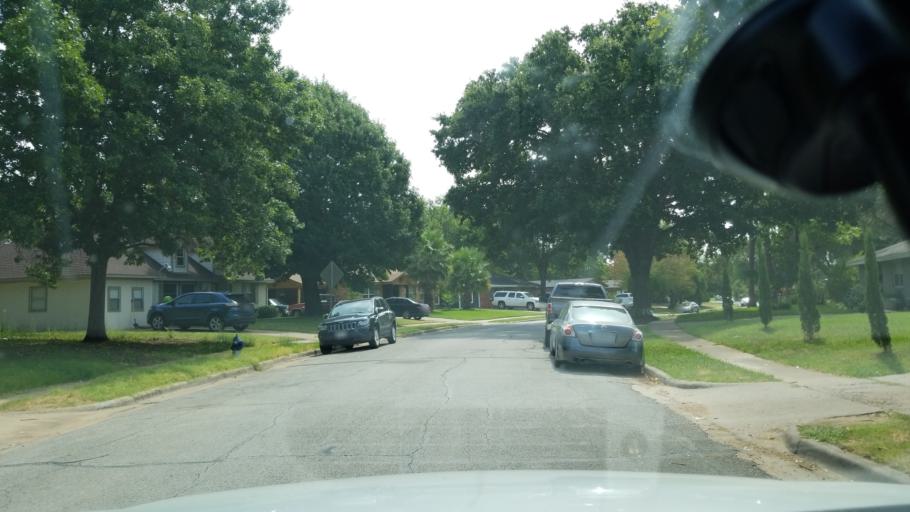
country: US
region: Texas
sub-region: Dallas County
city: Irving
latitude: 32.8258
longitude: -96.9787
